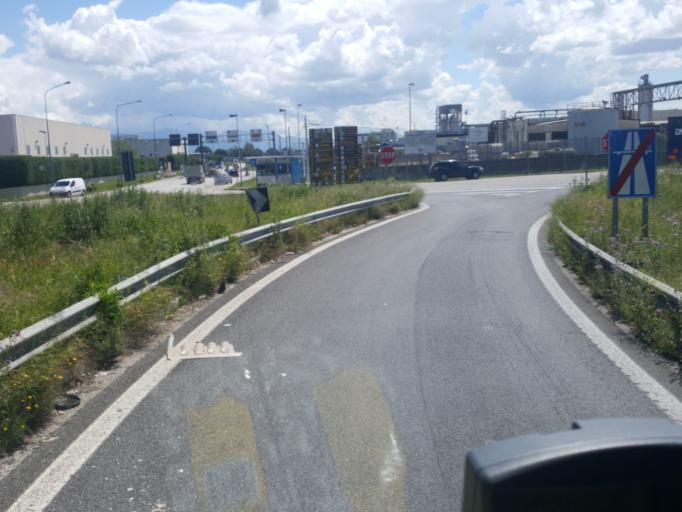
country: IT
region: Campania
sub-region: Provincia di Napoli
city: Pascarola
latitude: 40.9911
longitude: 14.2955
